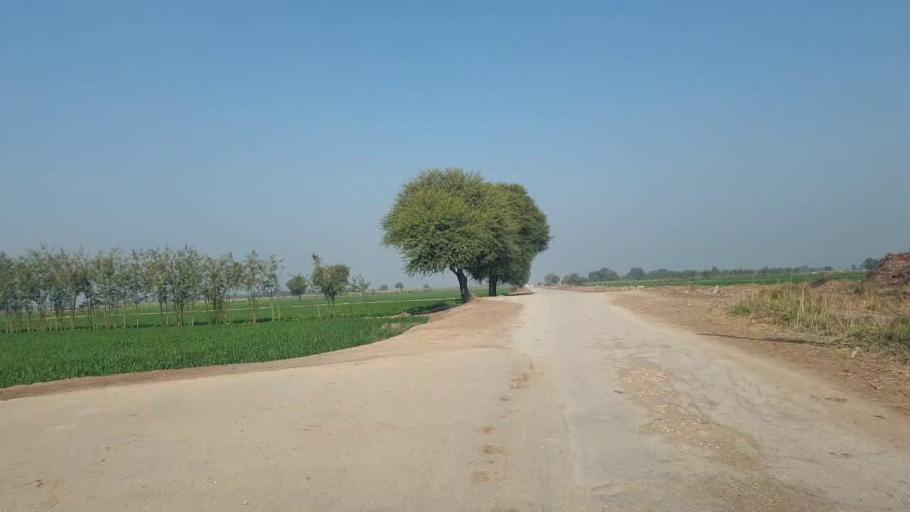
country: PK
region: Sindh
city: Shahdadpur
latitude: 25.9635
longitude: 68.5521
